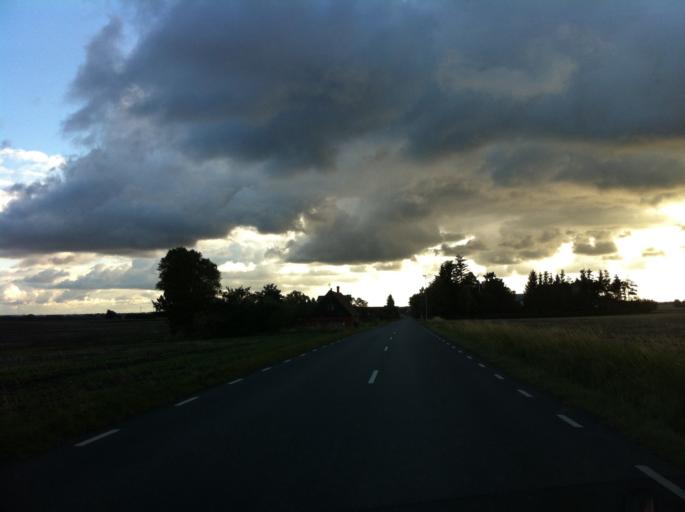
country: SE
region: Skane
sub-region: Svalovs Kommun
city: Svaloev
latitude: 55.8975
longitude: 13.1874
